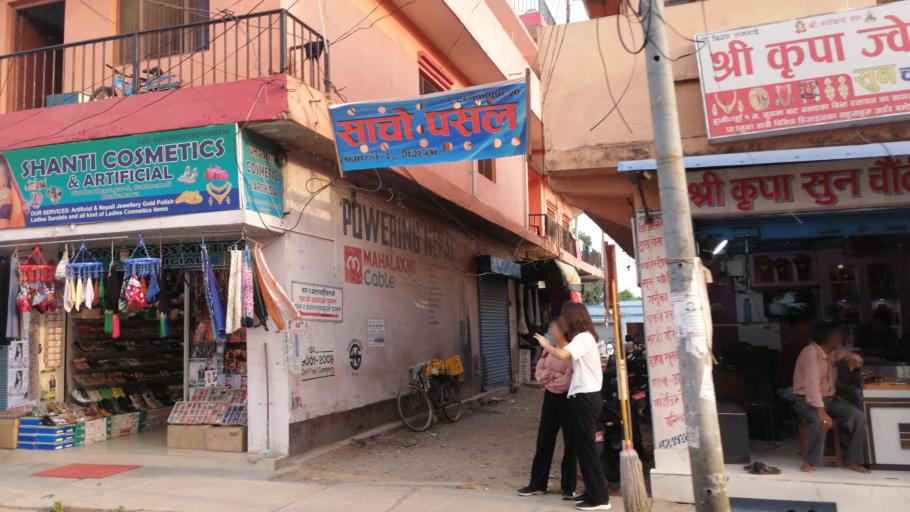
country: NP
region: Western Region
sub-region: Lumbini Zone
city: Bhairahawa
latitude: 27.5066
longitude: 83.4499
